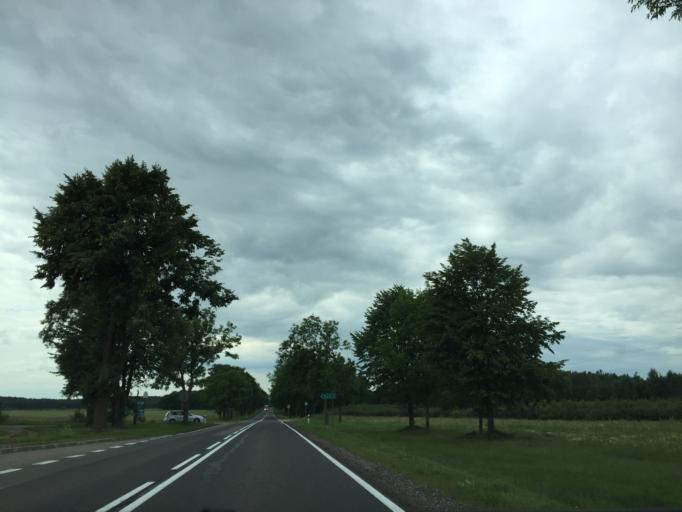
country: PL
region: Podlasie
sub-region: Powiat bielski
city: Bielsk Podlaski
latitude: 52.8856
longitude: 23.2136
